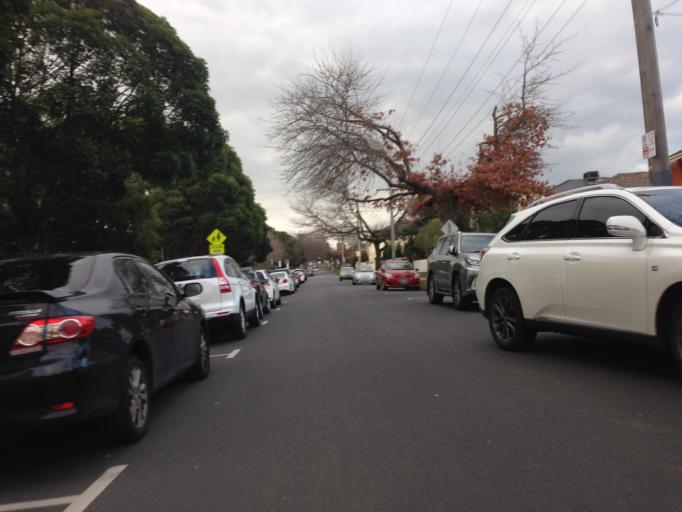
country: AU
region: Victoria
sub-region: Boroondara
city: Balwyn North
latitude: -37.7976
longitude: 145.0771
